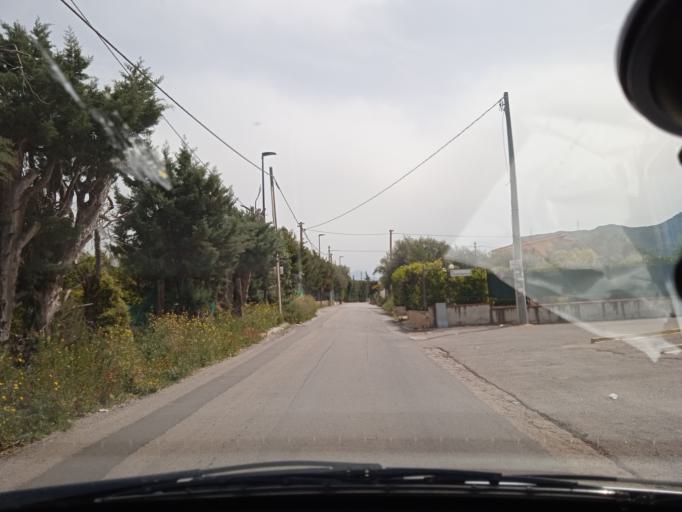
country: IT
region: Sicily
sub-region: Palermo
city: Torre Colonna-Sperone
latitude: 38.0345
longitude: 13.5629
